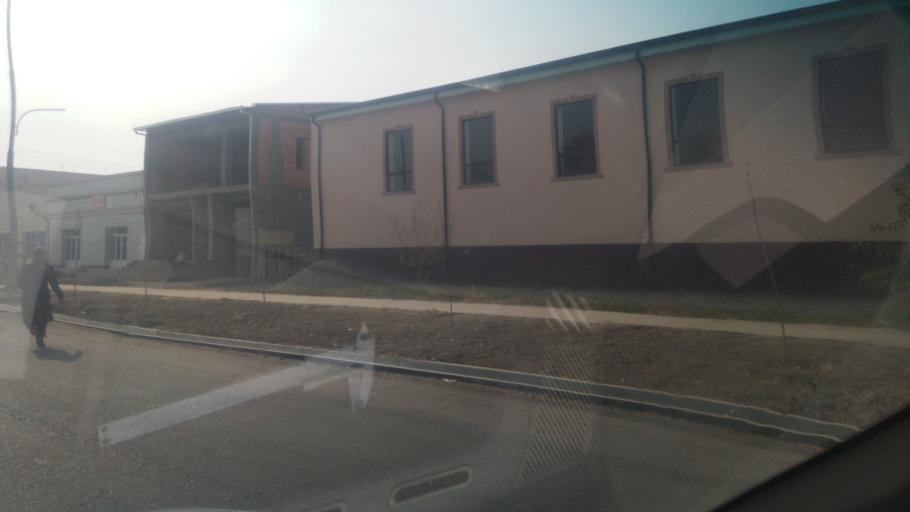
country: UZ
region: Sirdaryo
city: Guliston
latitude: 40.5058
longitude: 68.7741
